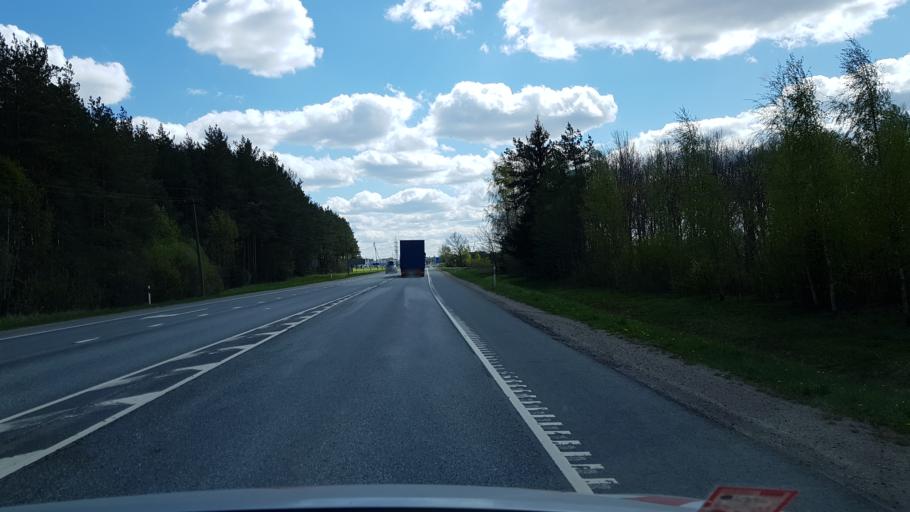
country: EE
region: Tartu
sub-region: Tartu linn
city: Tartu
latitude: 58.3866
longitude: 26.6693
